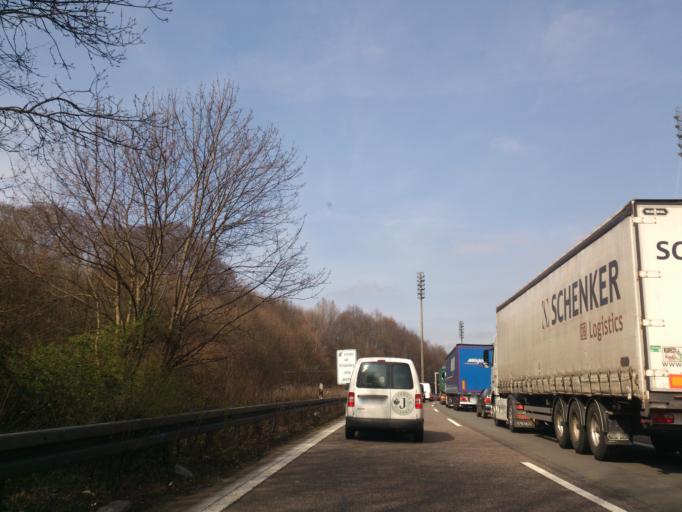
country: DE
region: North Rhine-Westphalia
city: Wulfrath
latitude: 51.2436
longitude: 7.0943
